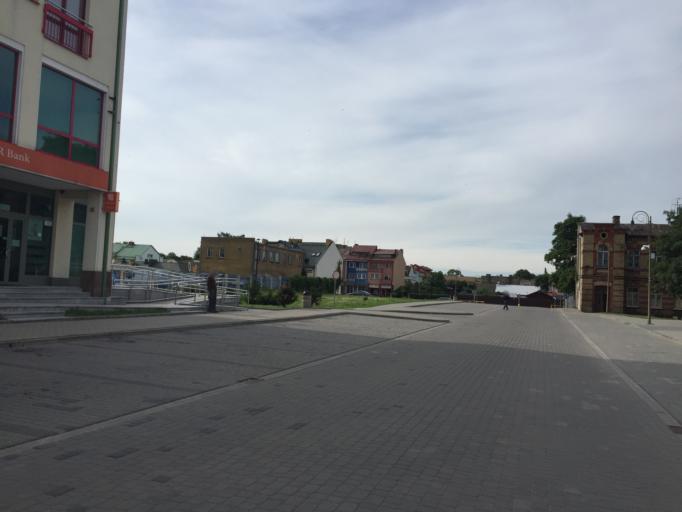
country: PL
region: Podlasie
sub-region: Suwalki
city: Suwalki
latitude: 54.1001
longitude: 22.9294
